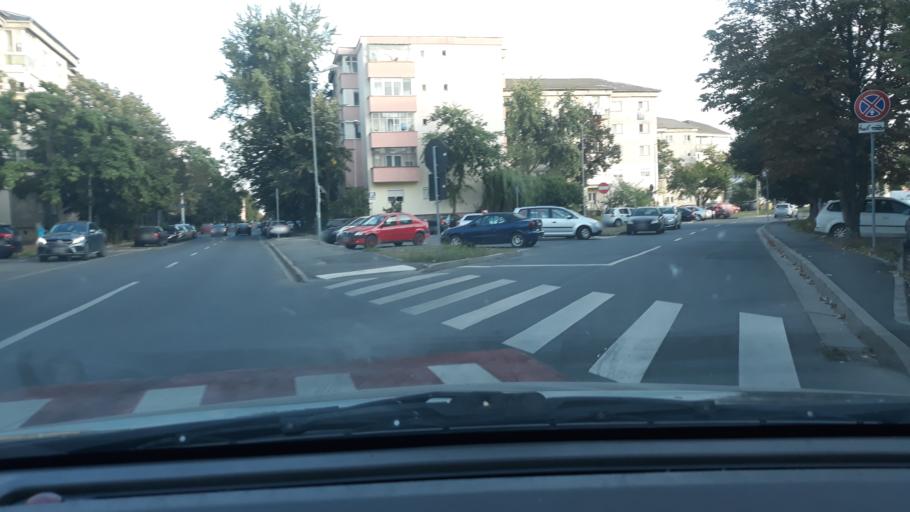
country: RO
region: Bihor
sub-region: Comuna Biharea
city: Oradea
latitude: 47.0345
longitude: 21.9445
